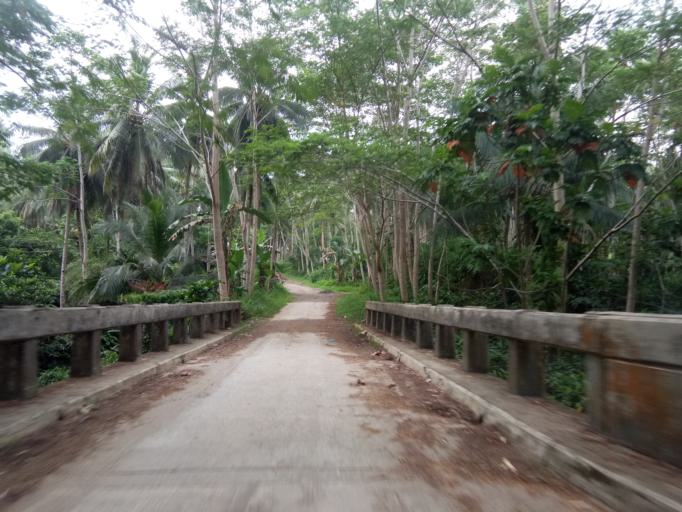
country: PH
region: Caraga
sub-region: Province of Surigao del Norte
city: Tubod
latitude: 9.5679
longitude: 125.5660
